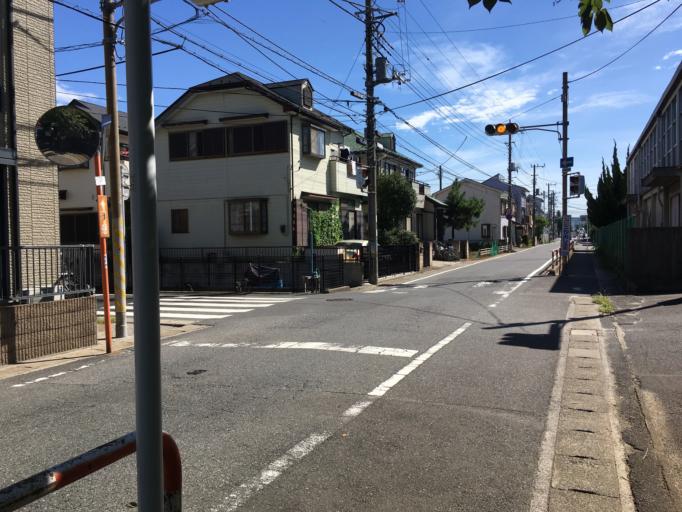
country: JP
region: Chiba
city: Matsudo
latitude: 35.7948
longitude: 139.8954
